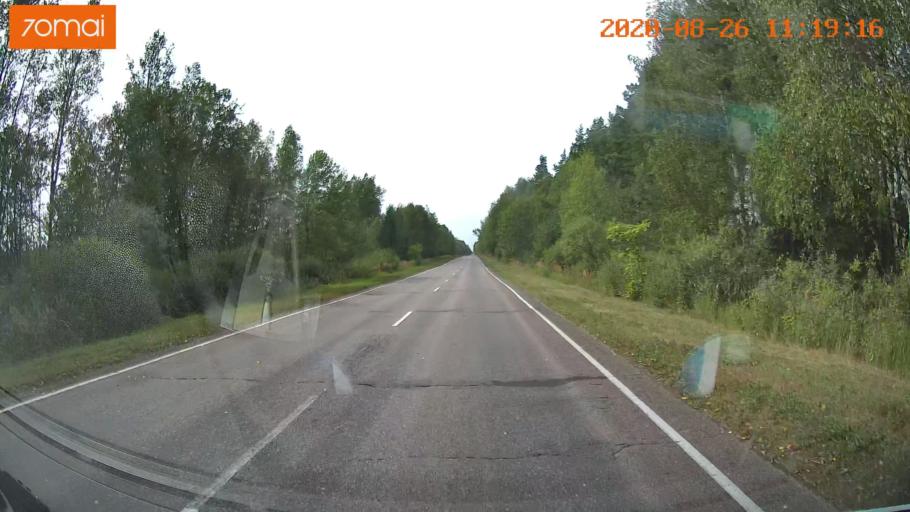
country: RU
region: Rjazan
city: Shilovo
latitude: 54.4010
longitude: 41.0827
